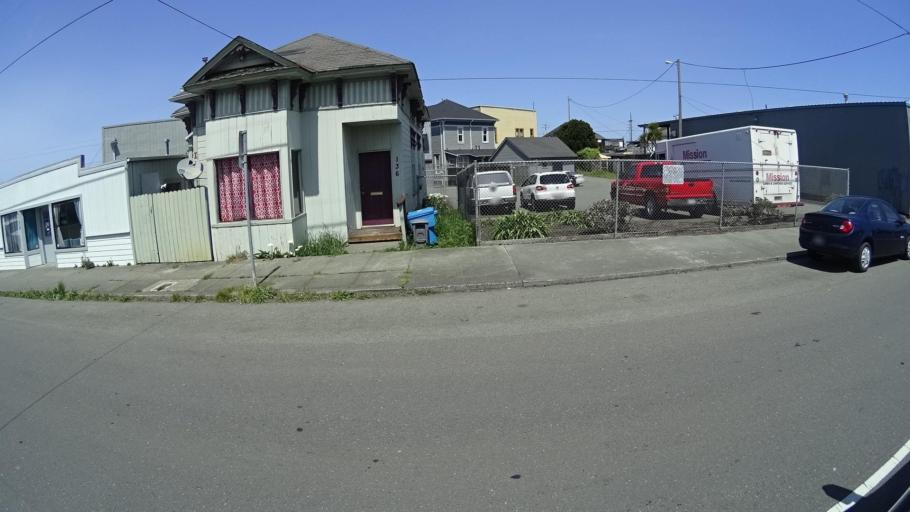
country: US
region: California
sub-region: Humboldt County
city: Eureka
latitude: 40.7993
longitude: -124.1728
